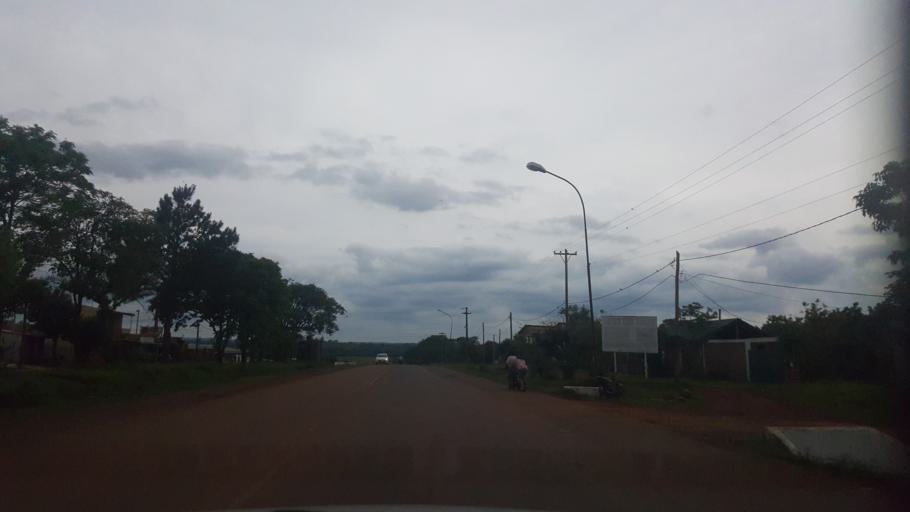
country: AR
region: Misiones
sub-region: Departamento de Candelaria
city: Candelaria
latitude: -27.4776
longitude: -55.7467
